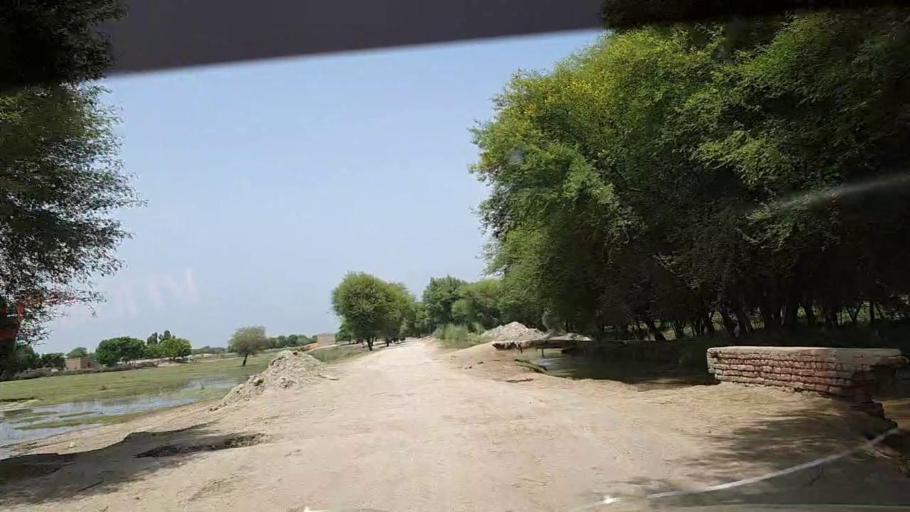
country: PK
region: Sindh
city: Khanpur
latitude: 27.8115
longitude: 69.4505
